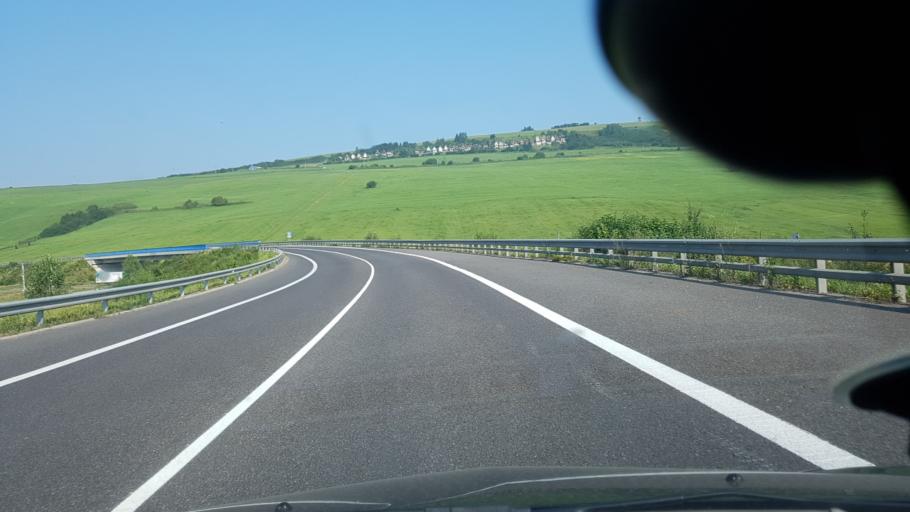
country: SK
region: Zilinsky
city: Tvrdosin
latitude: 49.3453
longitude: 19.5757
